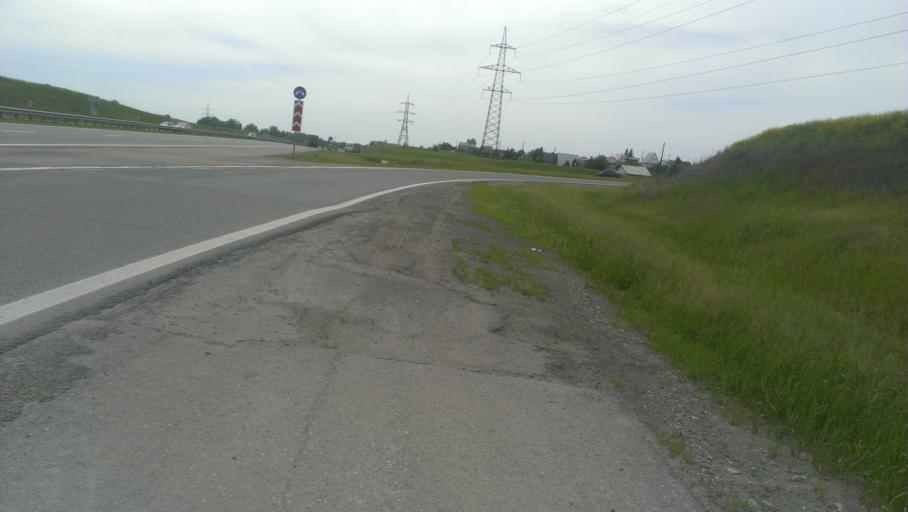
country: RU
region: Altai Krai
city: Sannikovo
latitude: 53.3405
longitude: 83.9356
